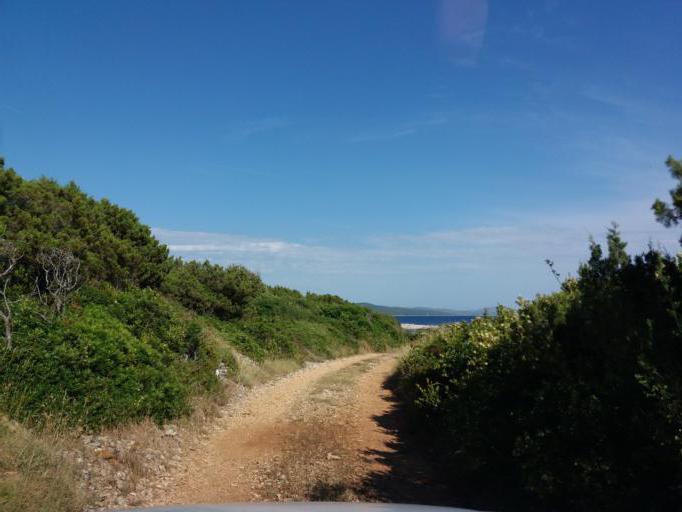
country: HR
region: Zadarska
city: Ugljan
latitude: 44.1260
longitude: 14.8700
